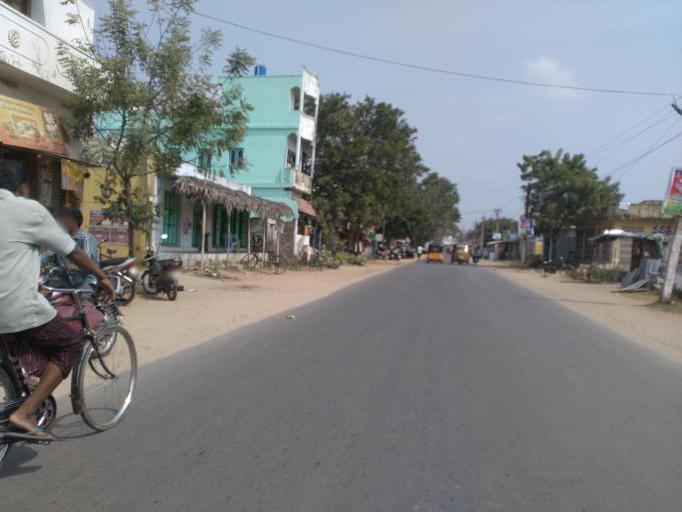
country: IN
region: Andhra Pradesh
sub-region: Prakasam
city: Chirala
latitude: 15.8483
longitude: 80.3849
